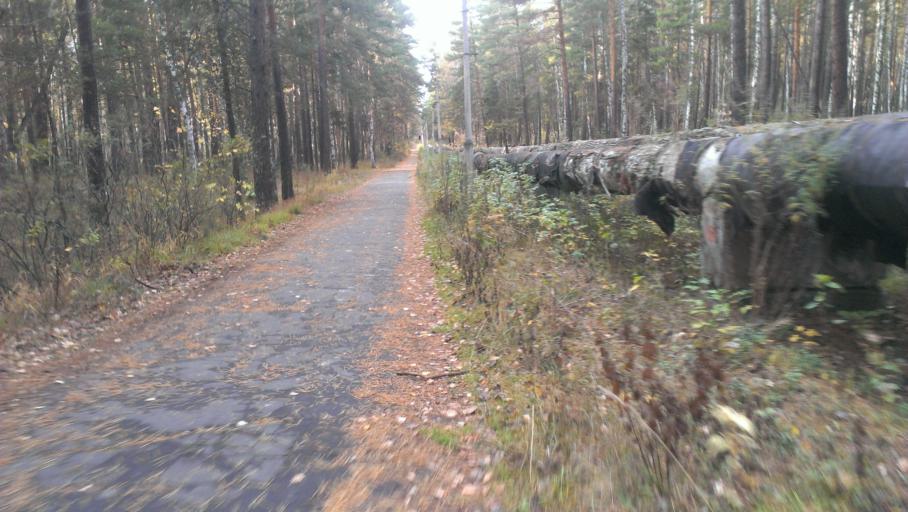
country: RU
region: Altai Krai
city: Yuzhnyy
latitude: 53.2663
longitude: 83.6839
